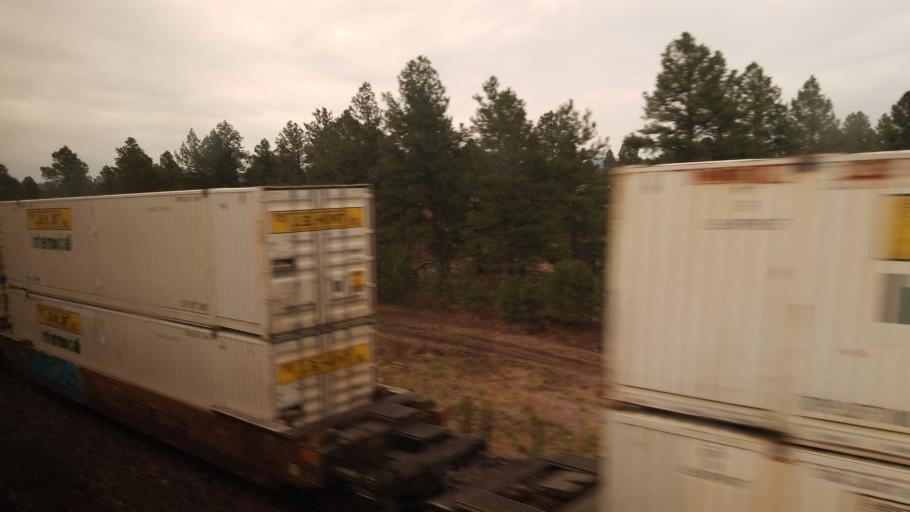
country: US
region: Arizona
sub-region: Coconino County
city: Parks
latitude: 35.2498
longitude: -111.9576
